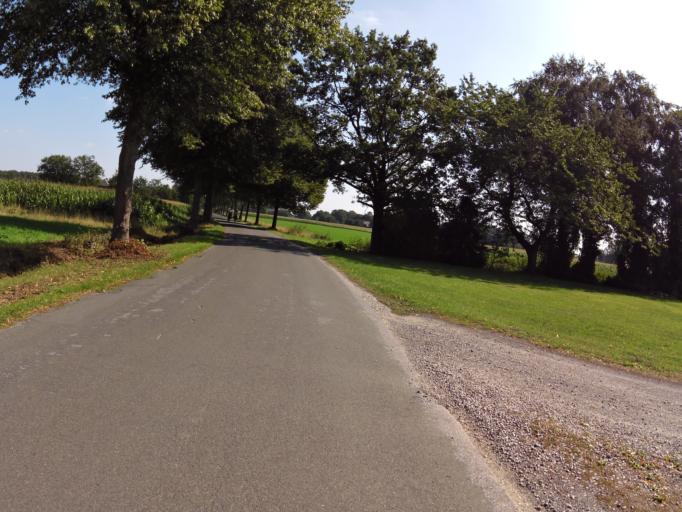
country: DE
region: North Rhine-Westphalia
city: Stadtlohn
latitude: 51.9994
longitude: 6.9534
